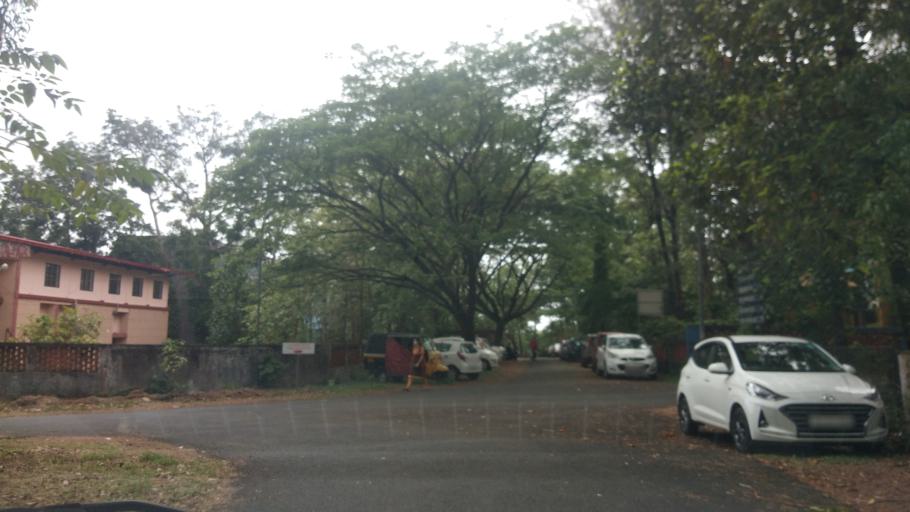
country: IN
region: Kerala
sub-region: Ernakulam
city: Elur
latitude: 10.0450
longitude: 76.3260
